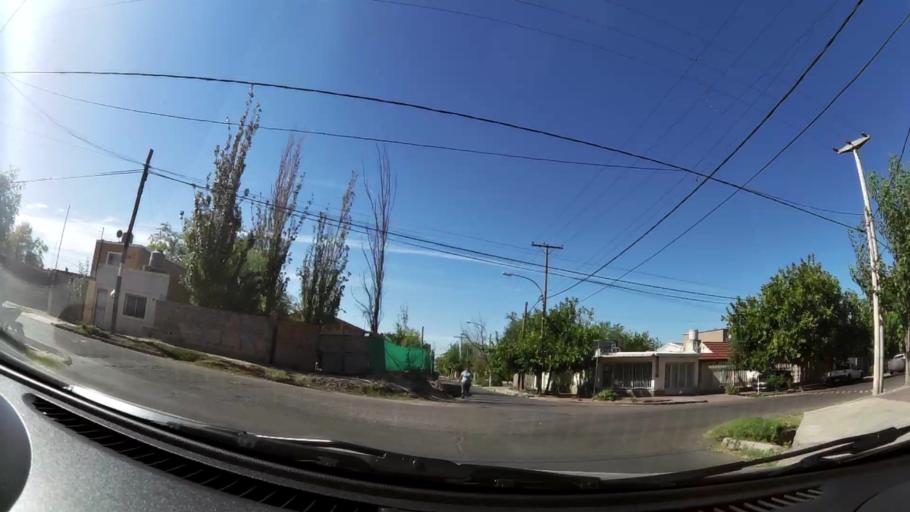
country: AR
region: Mendoza
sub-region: Departamento de Godoy Cruz
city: Godoy Cruz
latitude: -32.9417
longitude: -68.8094
